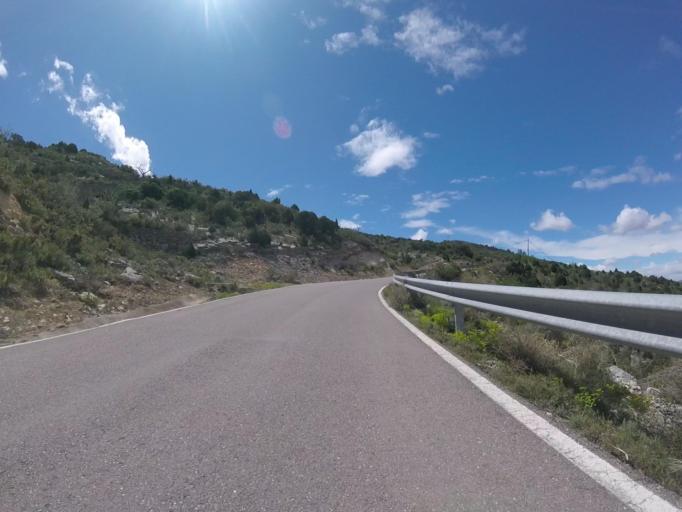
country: ES
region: Valencia
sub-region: Provincia de Castello
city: Sierra-Engarceran
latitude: 40.2816
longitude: -0.0316
